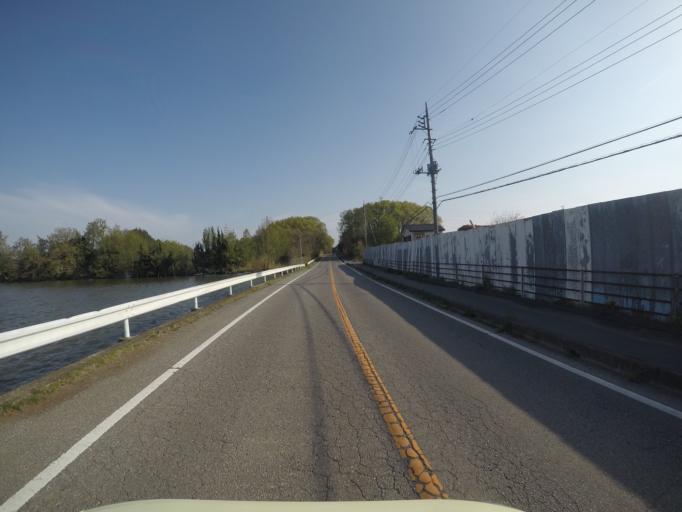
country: JP
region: Ibaraki
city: Ishige
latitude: 36.1803
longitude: 140.0180
